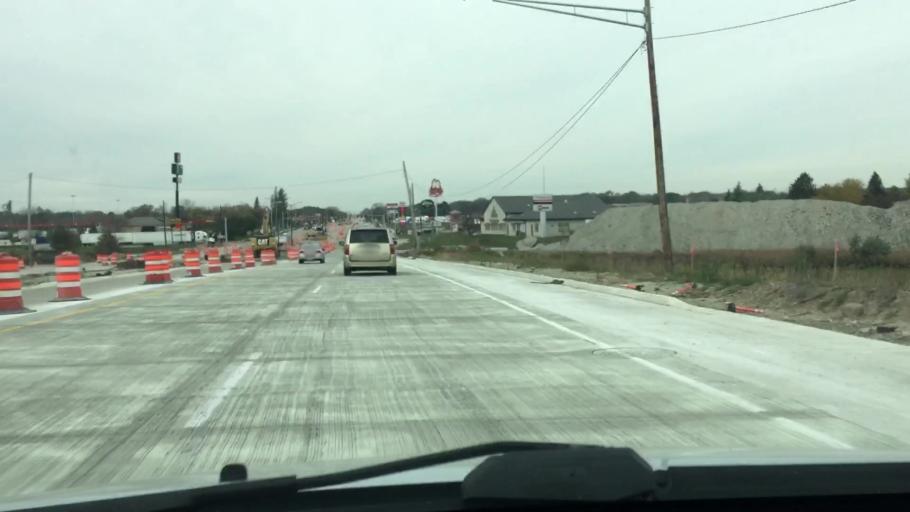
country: US
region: Wisconsin
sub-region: Racine County
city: Caledonia
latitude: 42.8727
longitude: -87.9391
